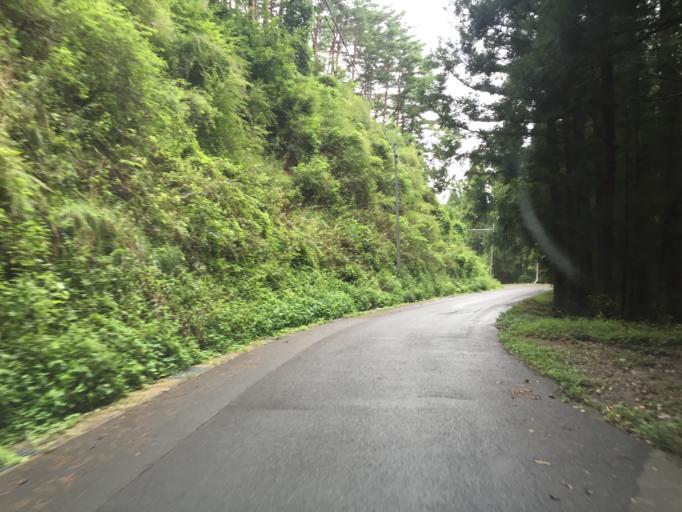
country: JP
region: Fukushima
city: Fukushima-shi
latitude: 37.7973
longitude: 140.3763
